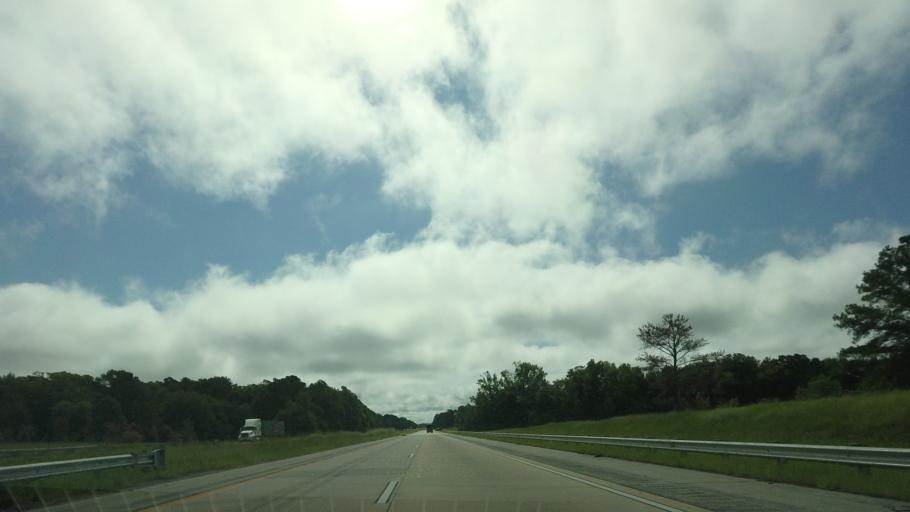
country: US
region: Georgia
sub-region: Twiggs County
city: Jeffersonville
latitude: 32.5980
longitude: -83.3125
